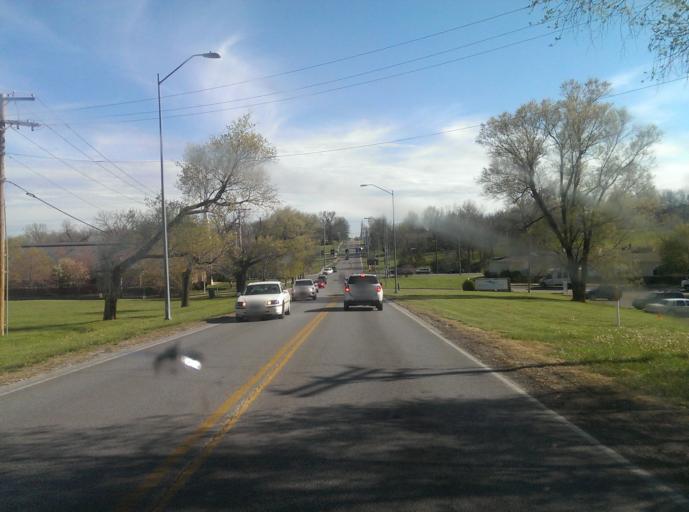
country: US
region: Missouri
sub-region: Jackson County
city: Grandview
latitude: 38.8919
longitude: -94.5952
